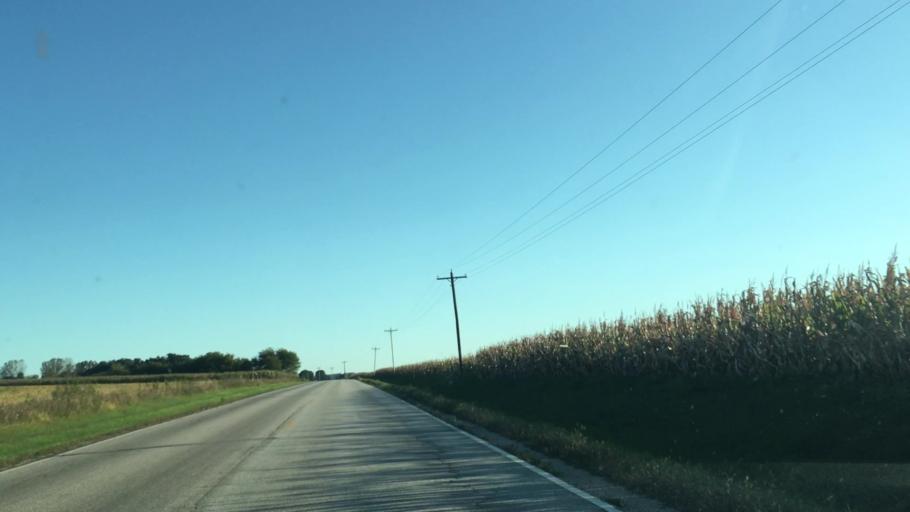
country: US
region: Minnesota
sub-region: Fillmore County
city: Chatfield
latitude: 43.8282
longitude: -92.0695
